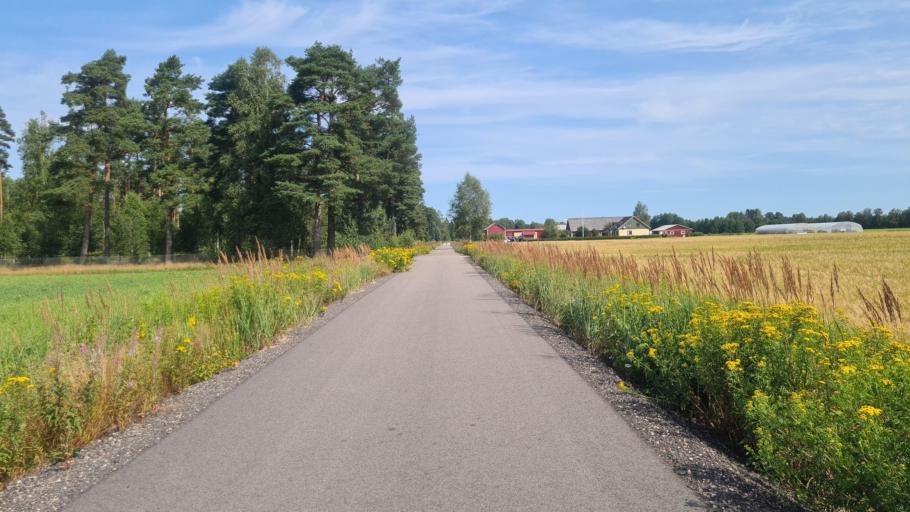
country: SE
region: Kronoberg
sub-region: Ljungby Kommun
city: Lagan
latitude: 56.9001
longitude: 13.9893
